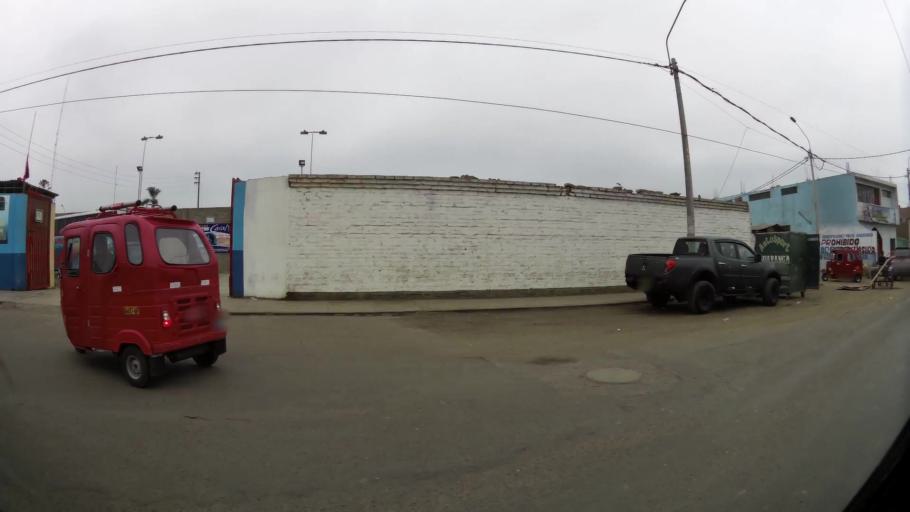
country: PE
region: Lima
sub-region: Barranca
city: Barranca
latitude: -10.7443
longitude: -77.7648
